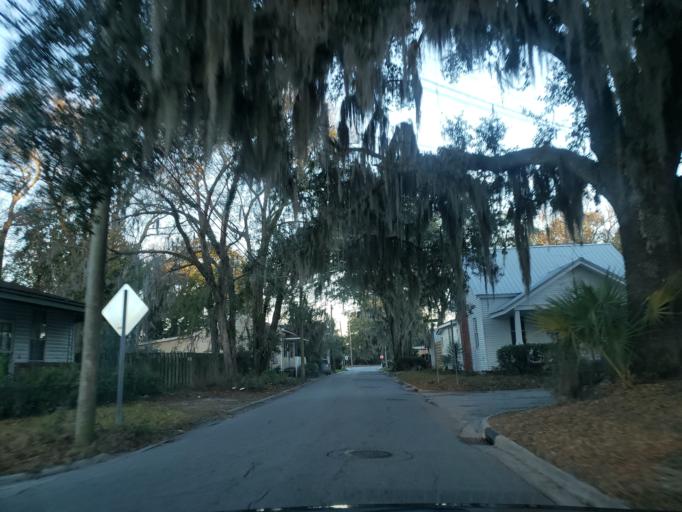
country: US
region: Georgia
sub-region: Chatham County
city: Savannah
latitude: 32.0433
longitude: -81.1085
